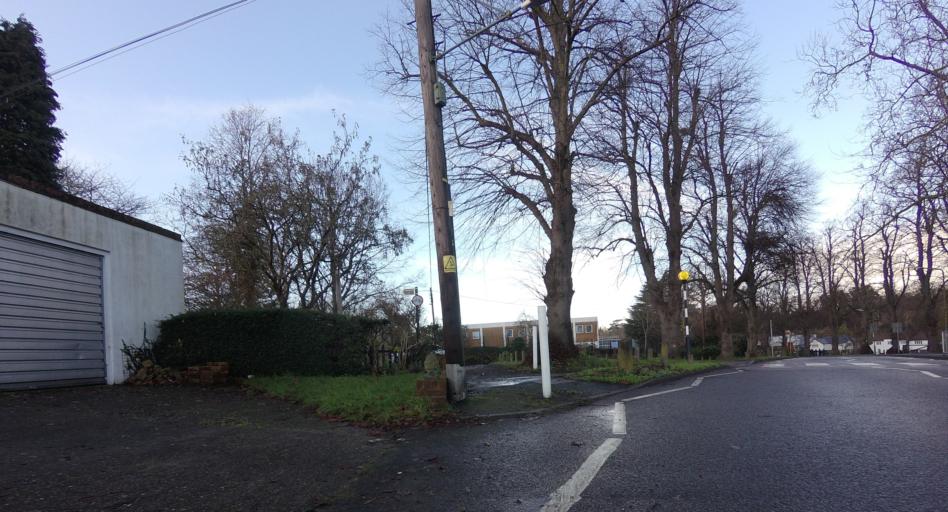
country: GB
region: England
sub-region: Kent
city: Dartford
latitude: 51.4277
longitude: 0.1963
